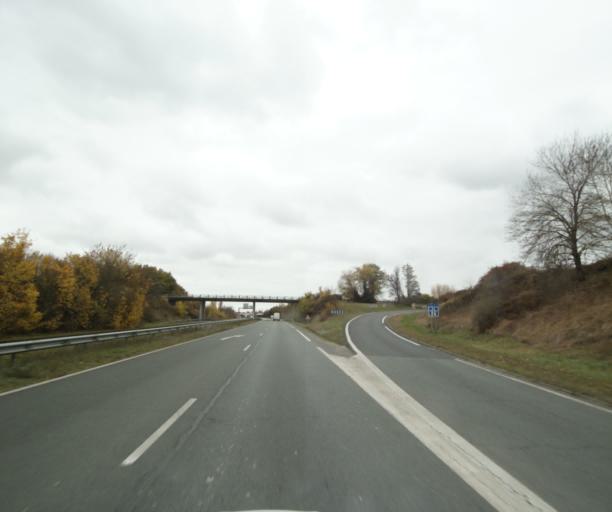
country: FR
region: Poitou-Charentes
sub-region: Departement de la Charente-Maritime
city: Saintes
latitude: 45.7523
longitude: -0.6595
